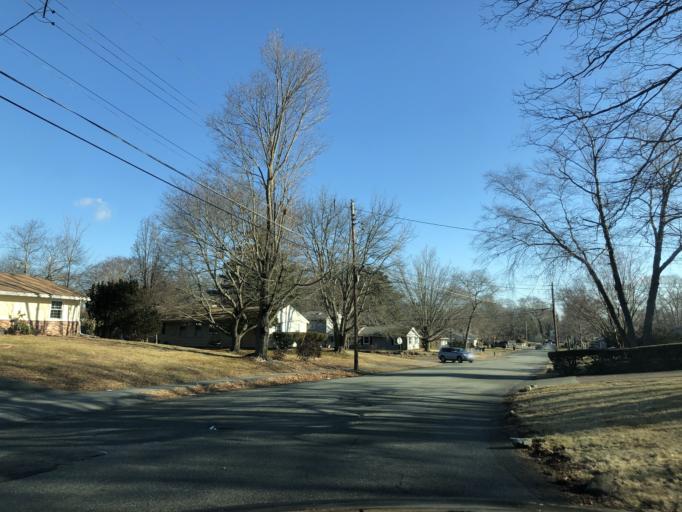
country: US
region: Massachusetts
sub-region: Plymouth County
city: Brockton
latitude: 42.1055
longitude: -71.0011
